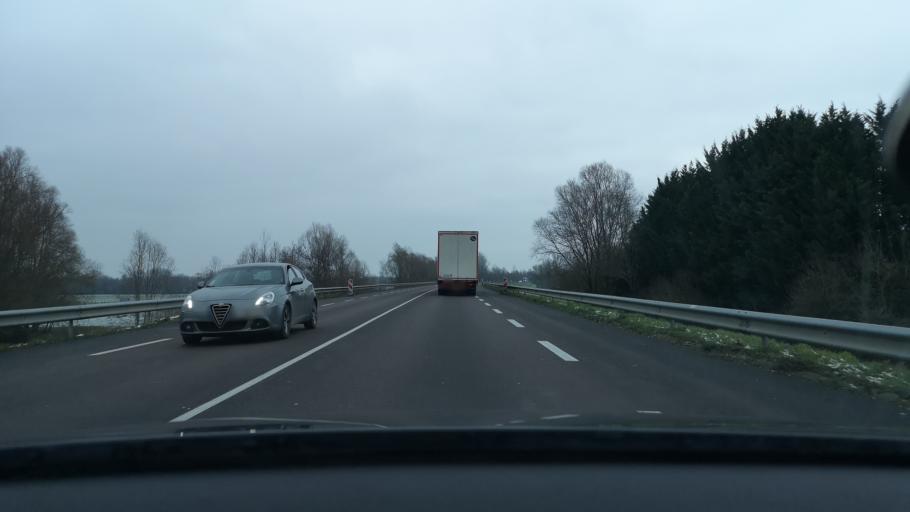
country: FR
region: Bourgogne
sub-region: Departement de Saone-et-Loire
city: Saint-Marcel
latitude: 46.7829
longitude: 4.8872
